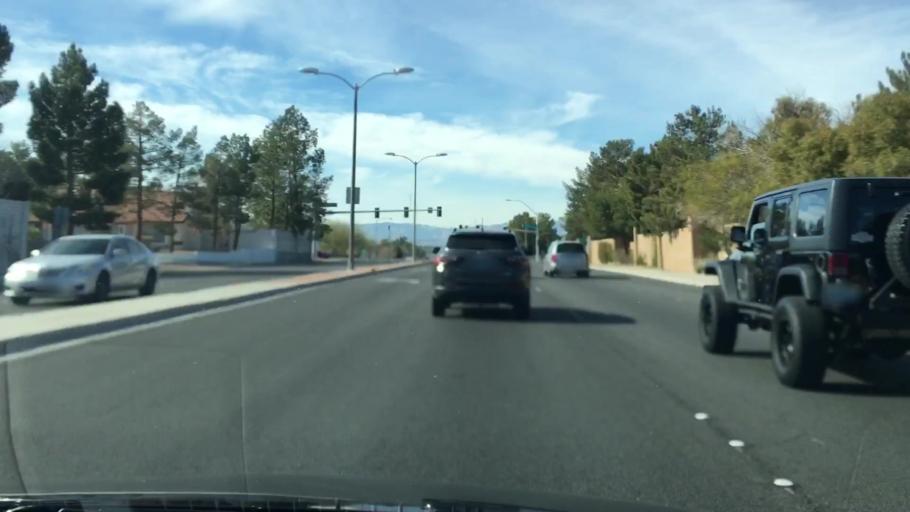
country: US
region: Nevada
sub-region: Clark County
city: Whitney
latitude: 36.0571
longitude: -115.0990
